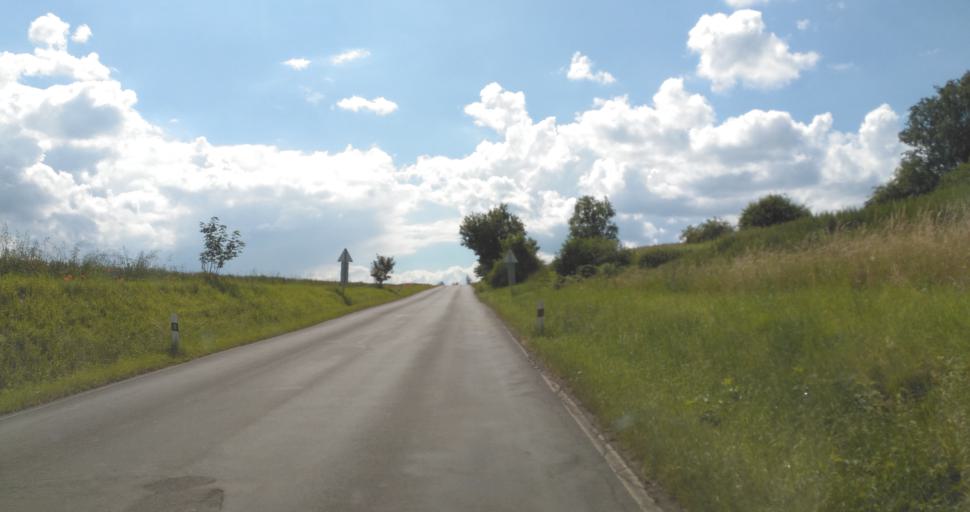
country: CZ
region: Central Bohemia
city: Lochovice
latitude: 49.8483
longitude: 13.9724
